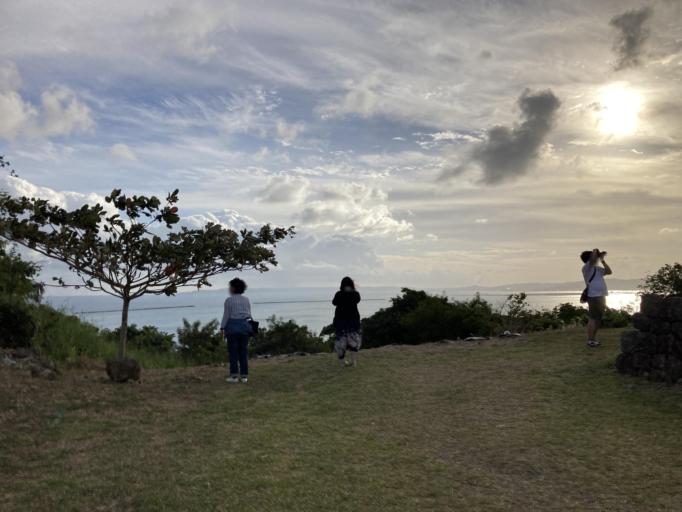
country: JP
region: Okinawa
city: Katsuren-haebaru
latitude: 26.3299
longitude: 127.8795
